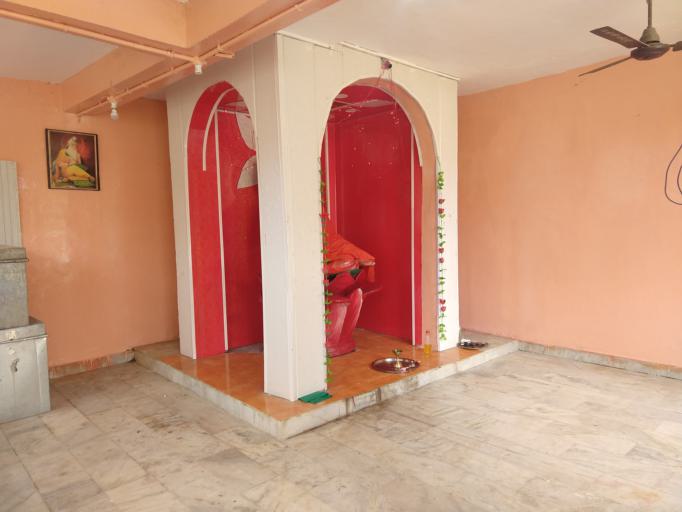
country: IN
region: Himachal Pradesh
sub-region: Kangra
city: Palampur
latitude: 32.1101
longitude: 76.5336
